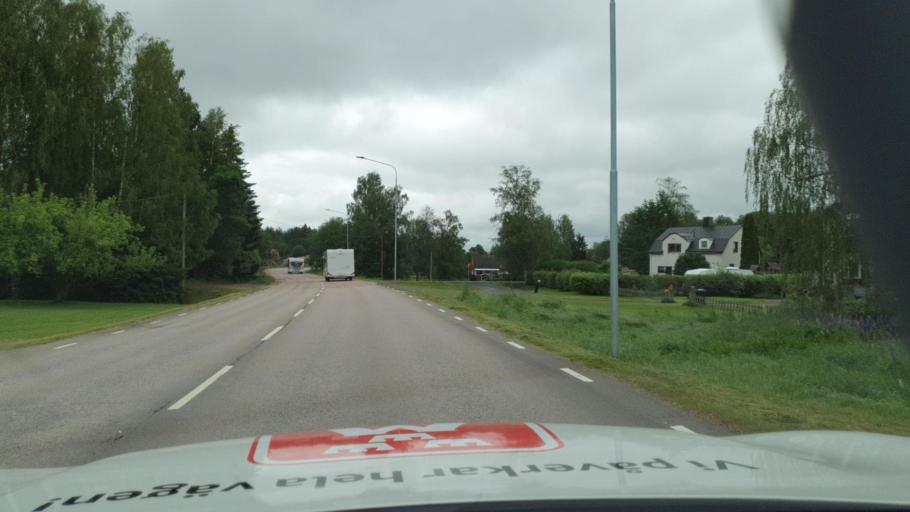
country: SE
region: Vaermland
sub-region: Karlstads Kommun
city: Valberg
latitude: 59.3852
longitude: 13.1787
